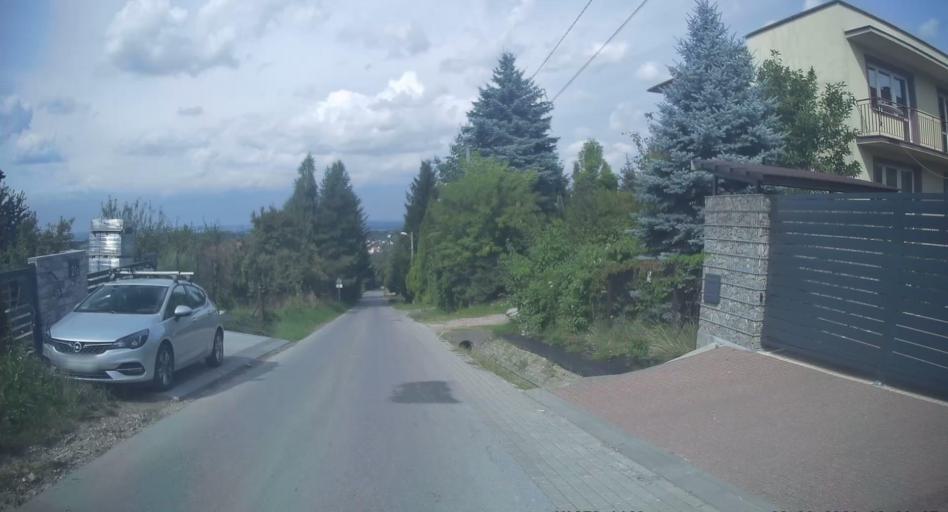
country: PL
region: Lesser Poland Voivodeship
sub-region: Powiat wielicki
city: Wieliczka
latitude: 49.9770
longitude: 20.0553
